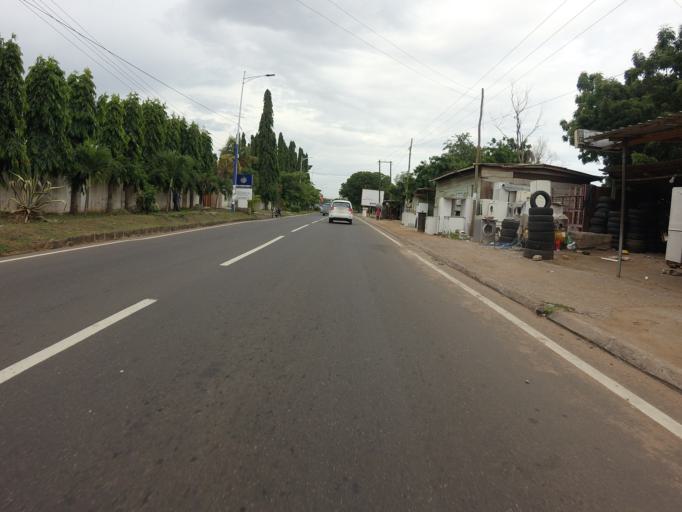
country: GH
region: Greater Accra
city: Dome
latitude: 5.6090
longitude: -0.2128
